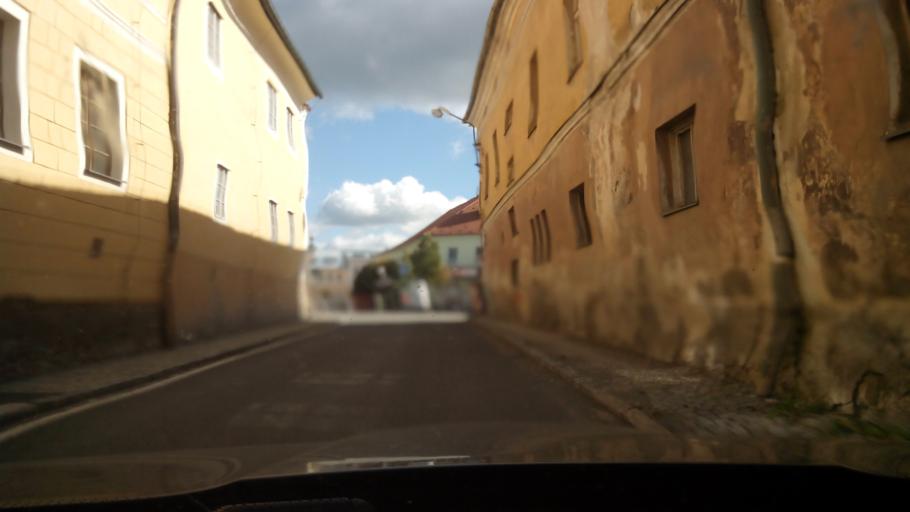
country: CZ
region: Plzensky
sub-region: Okres Klatovy
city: Kasperske Hory
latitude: 49.1440
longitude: 13.5541
